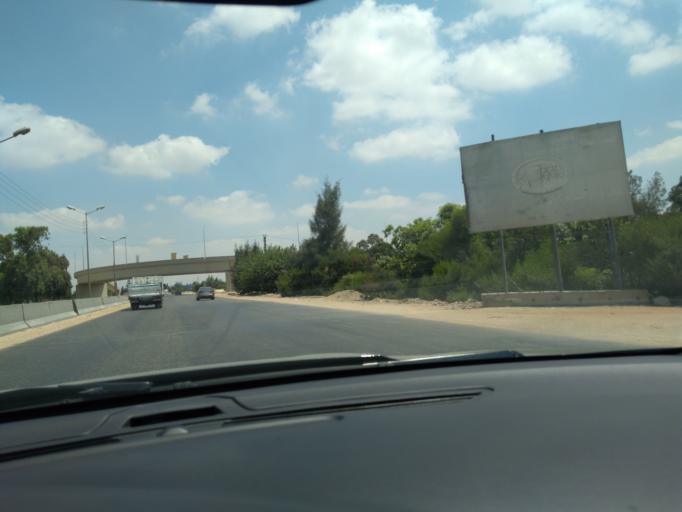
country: EG
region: Al Isma'iliyah
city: Ismailia
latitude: 30.6653
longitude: 32.2697
